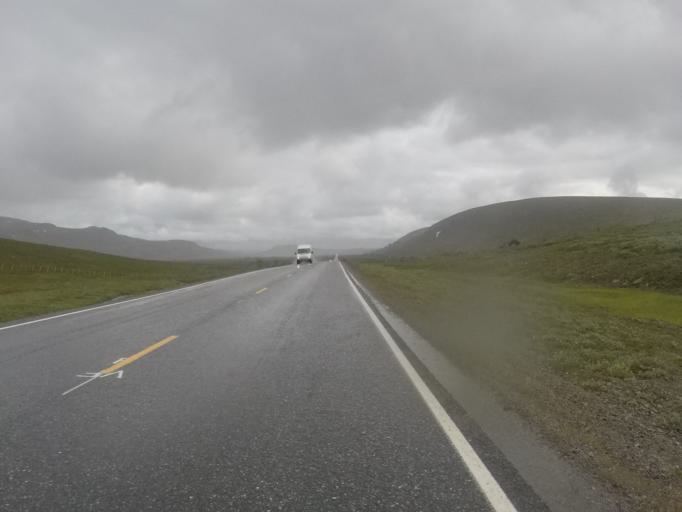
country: NO
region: Finnmark Fylke
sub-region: Kvalsund
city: Kvalsund
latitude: 70.1695
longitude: 23.7635
